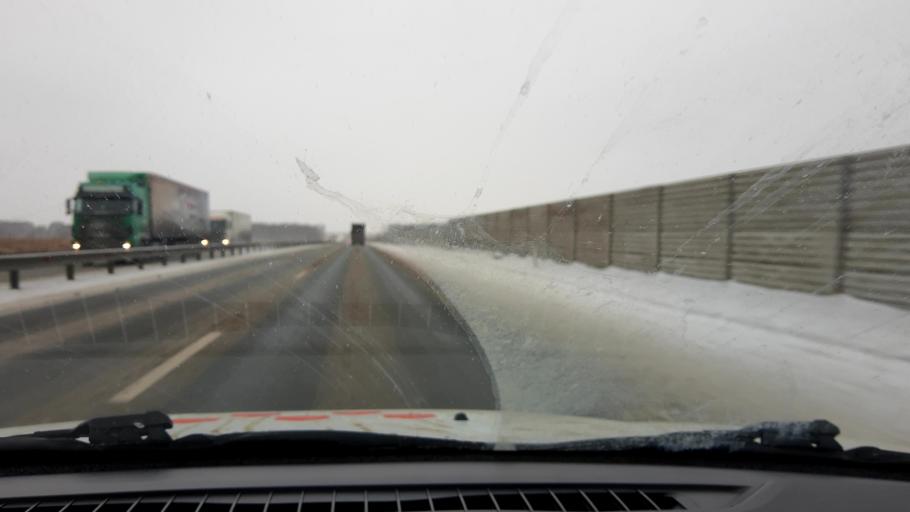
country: RU
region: Nizjnij Novgorod
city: Burevestnik
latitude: 56.1112
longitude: 43.9723
